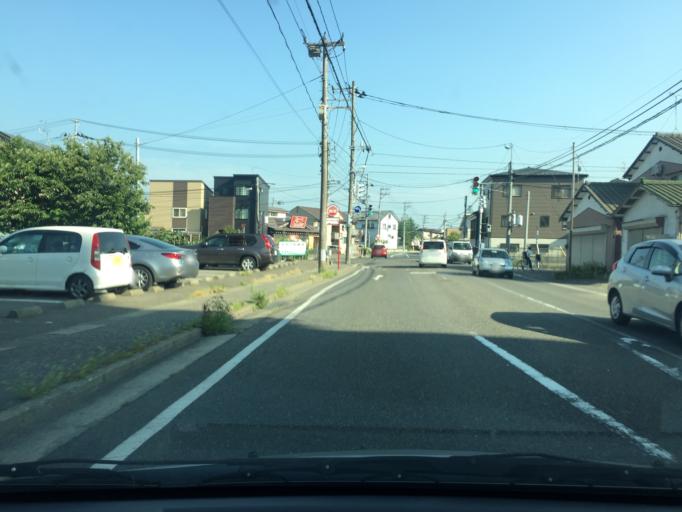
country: JP
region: Niigata
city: Niigata-shi
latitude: 37.8882
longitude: 139.0404
